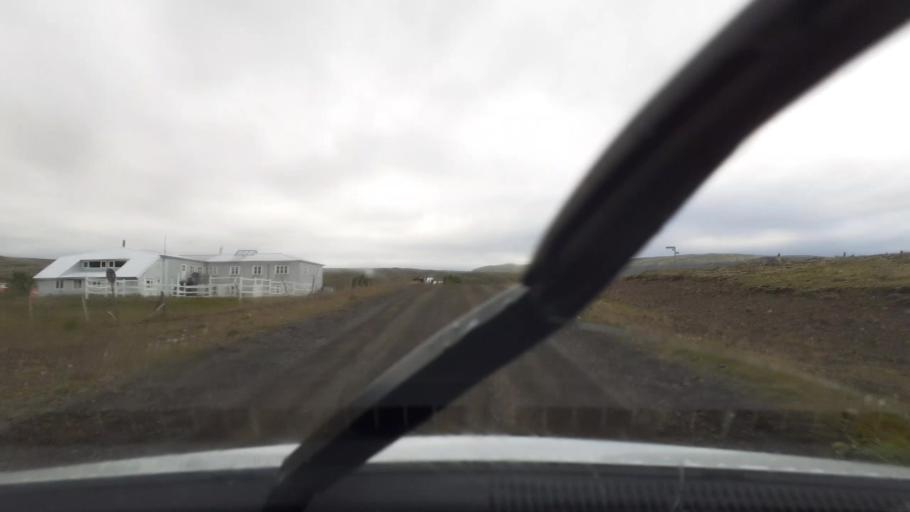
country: IS
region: Capital Region
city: Mosfellsbaer
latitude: 64.2051
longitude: -21.5624
